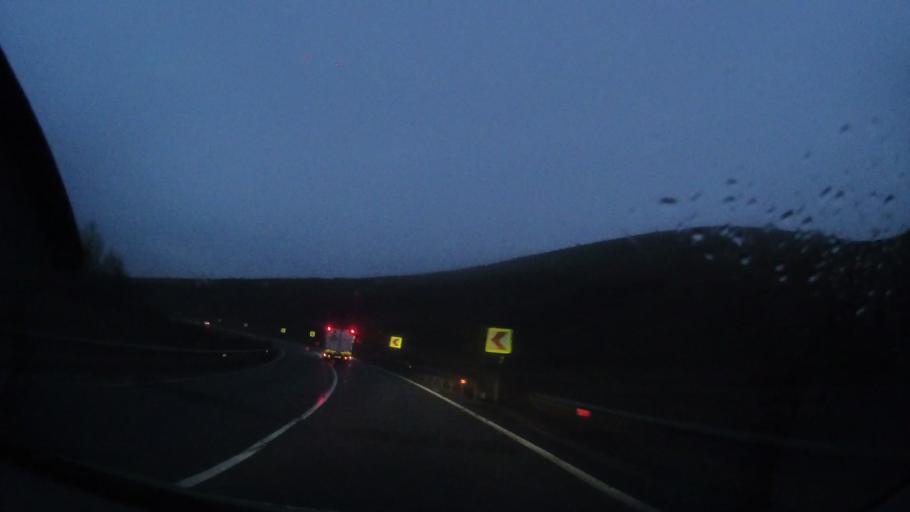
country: RO
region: Harghita
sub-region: Comuna Subcetate
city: Subcetate
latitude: 46.8397
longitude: 25.4835
